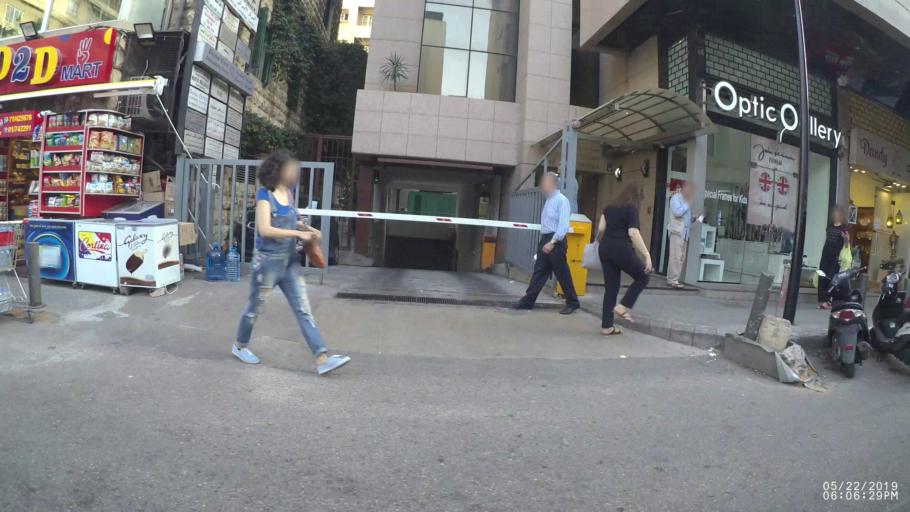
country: LB
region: Beyrouth
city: Ra's Bayrut
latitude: 33.8969
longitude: 35.4851
